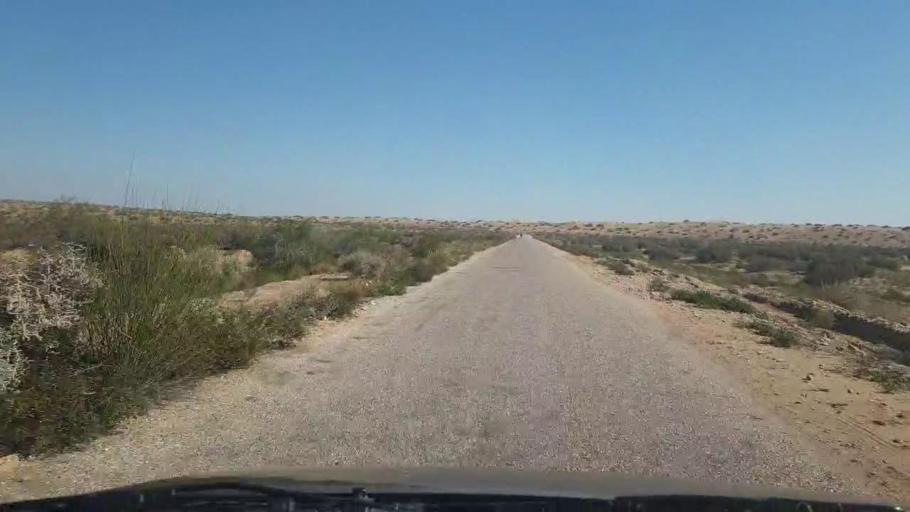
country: PK
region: Sindh
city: Bozdar
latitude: 27.0002
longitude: 68.8279
